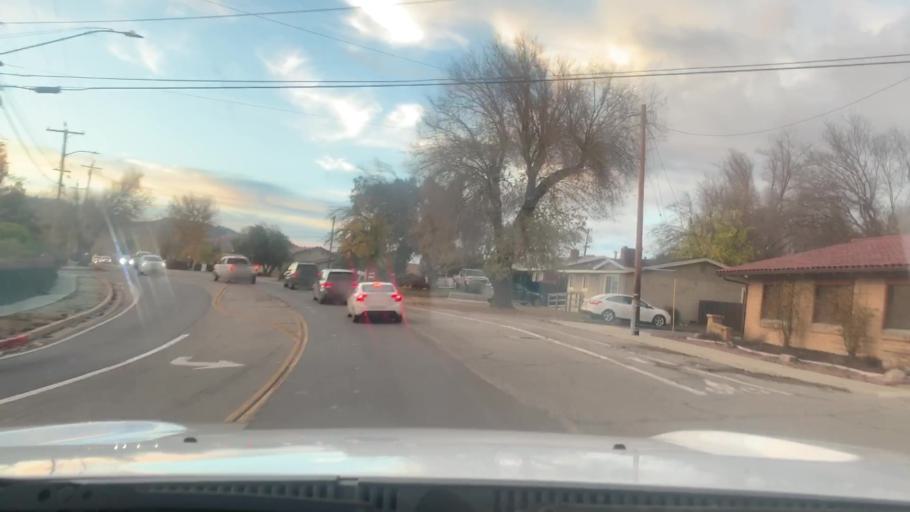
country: US
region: California
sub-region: San Luis Obispo County
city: Paso Robles
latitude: 35.6286
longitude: -120.6757
